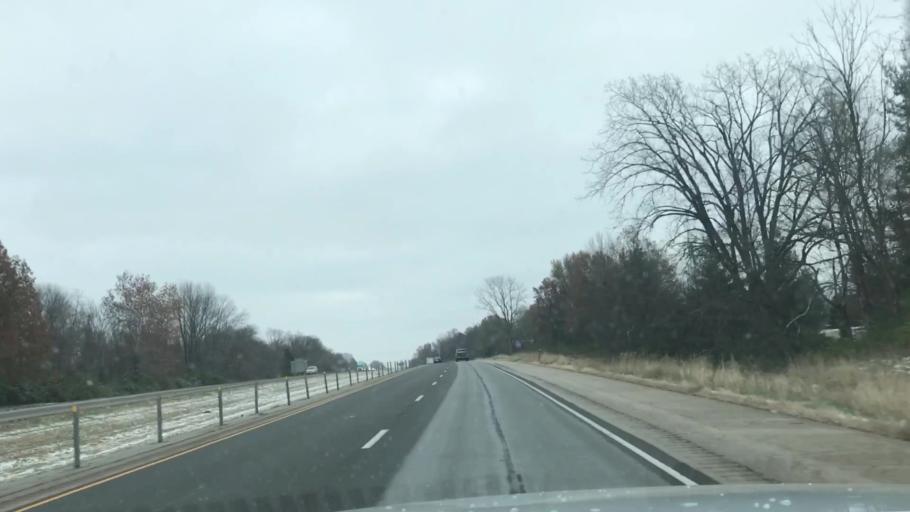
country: US
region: Illinois
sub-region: Madison County
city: Maryville
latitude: 38.7537
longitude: -89.9480
